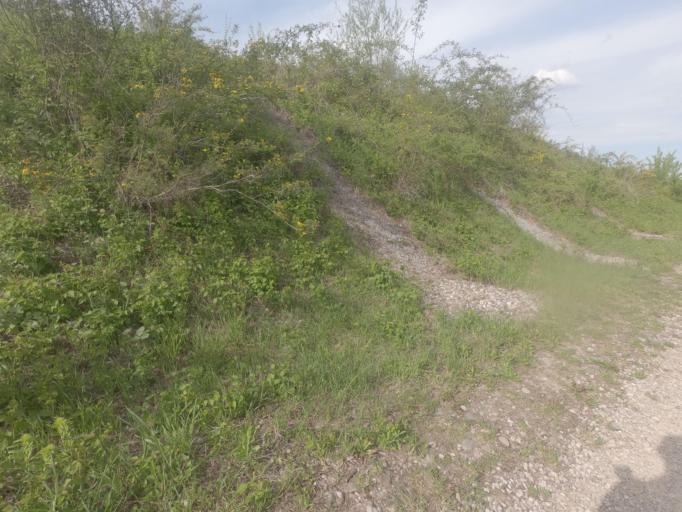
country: CH
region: Bern
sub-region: Oberaargau
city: Attiswil
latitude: 47.2315
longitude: 7.5991
